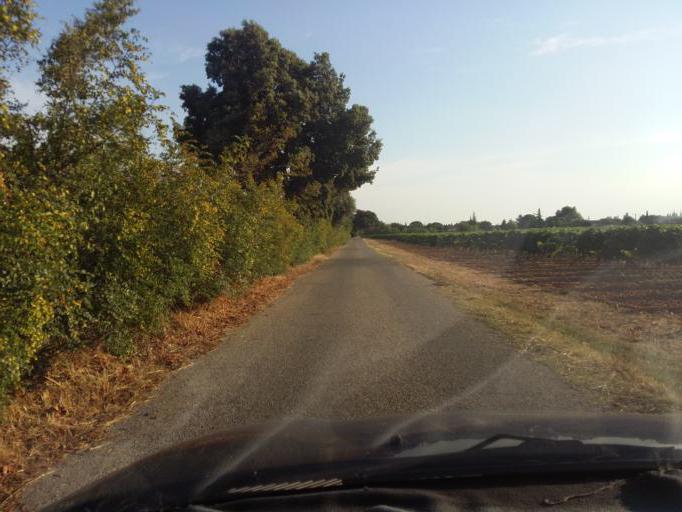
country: FR
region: Provence-Alpes-Cote d'Azur
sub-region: Departement du Vaucluse
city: Carpentras
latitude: 44.0762
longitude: 5.0648
